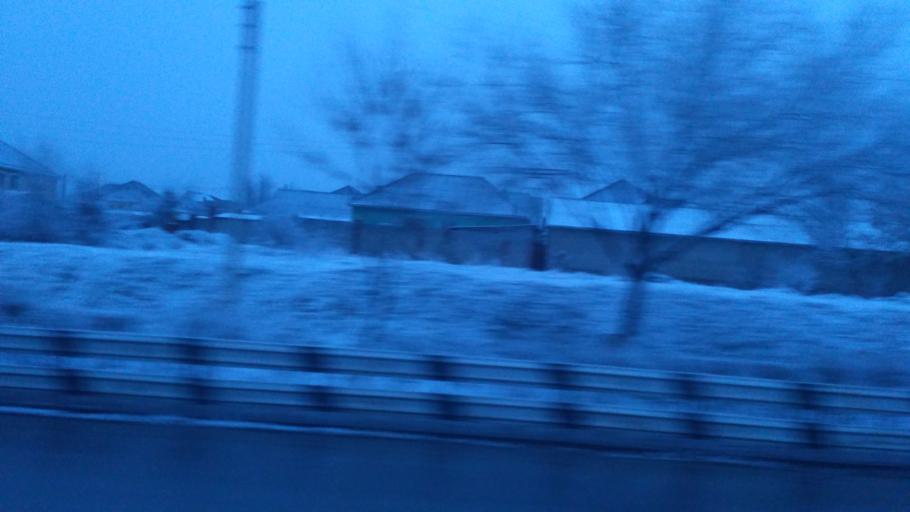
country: KZ
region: Ongtustik Qazaqstan
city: Shymkent
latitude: 42.3568
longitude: 69.5239
